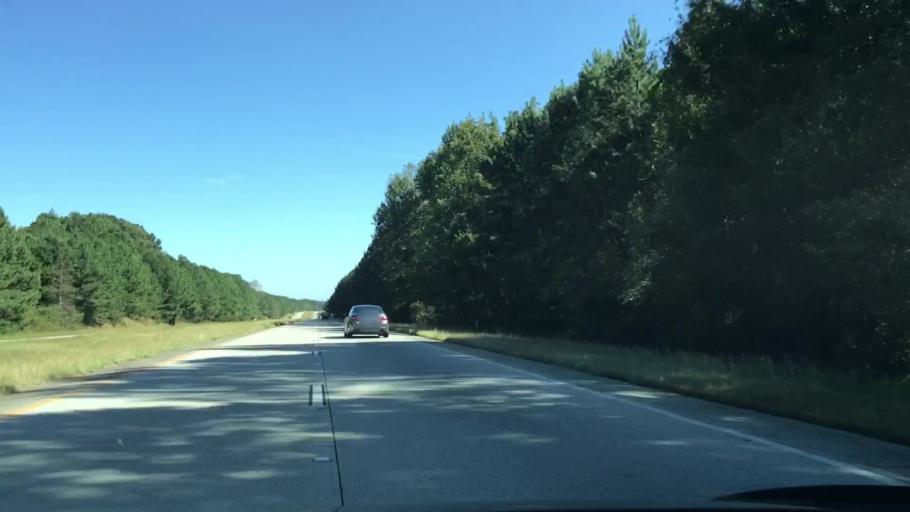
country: US
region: Georgia
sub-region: Oconee County
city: Bogart
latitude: 33.9379
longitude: -83.5479
